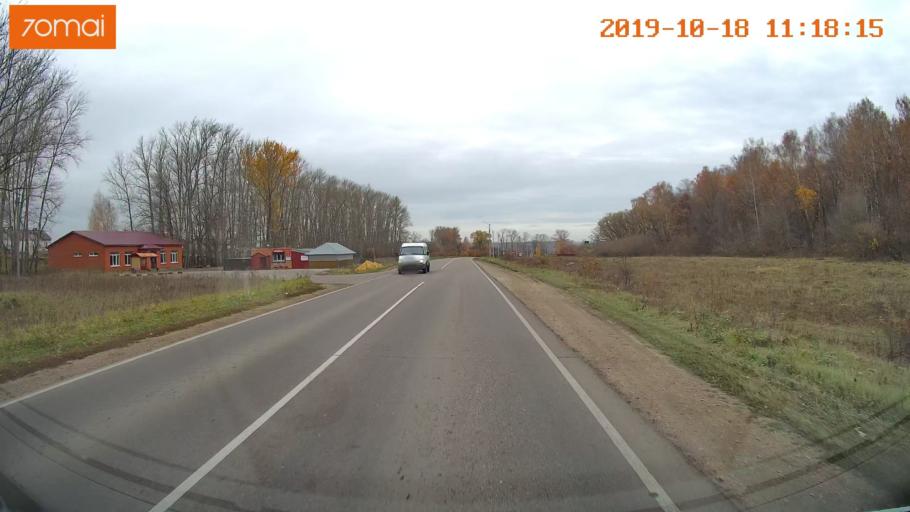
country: RU
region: Tula
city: Kimovsk
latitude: 54.0370
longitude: 38.5503
